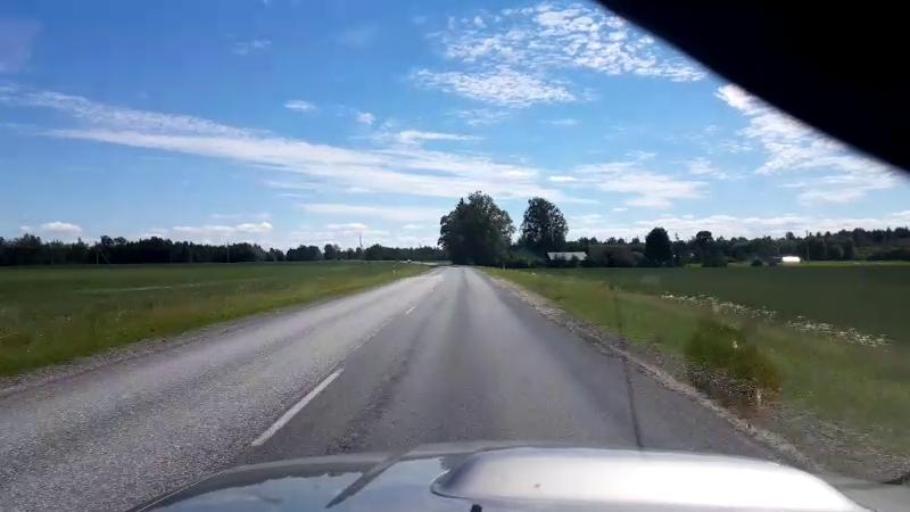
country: EE
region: Laeaene-Virumaa
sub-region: Rakke vald
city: Rakke
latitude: 58.8904
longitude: 26.2860
